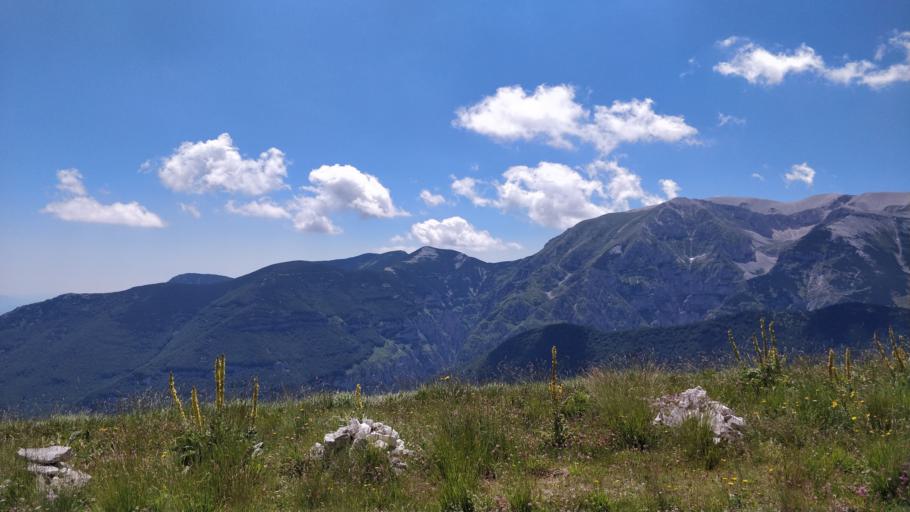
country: IT
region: Abruzzo
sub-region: Provincia di Chieti
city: Pretoro
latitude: 42.1583
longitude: 14.1293
